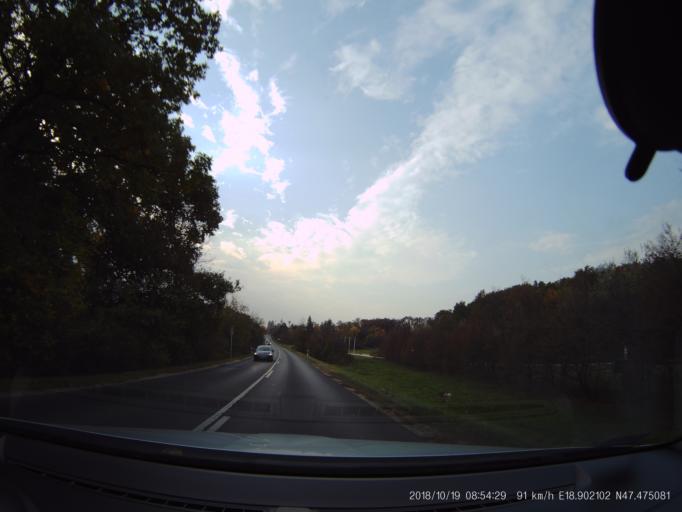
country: HU
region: Pest
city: Budakeszi
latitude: 47.4750
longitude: 18.9021
